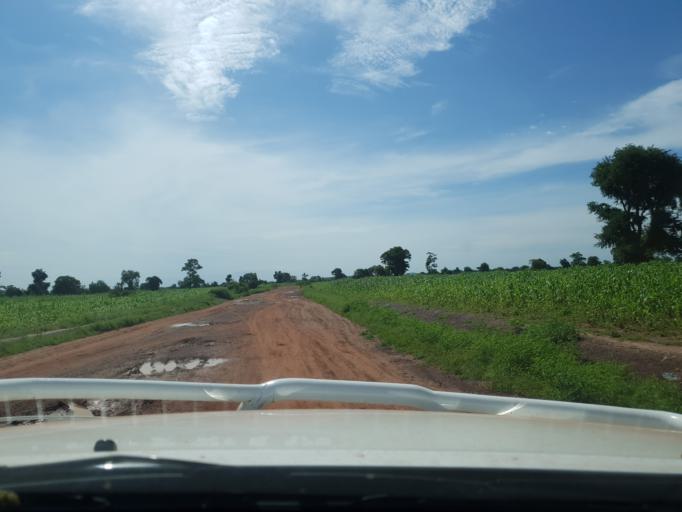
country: ML
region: Koulikoro
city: Banamba
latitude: 13.2811
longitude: -7.5540
